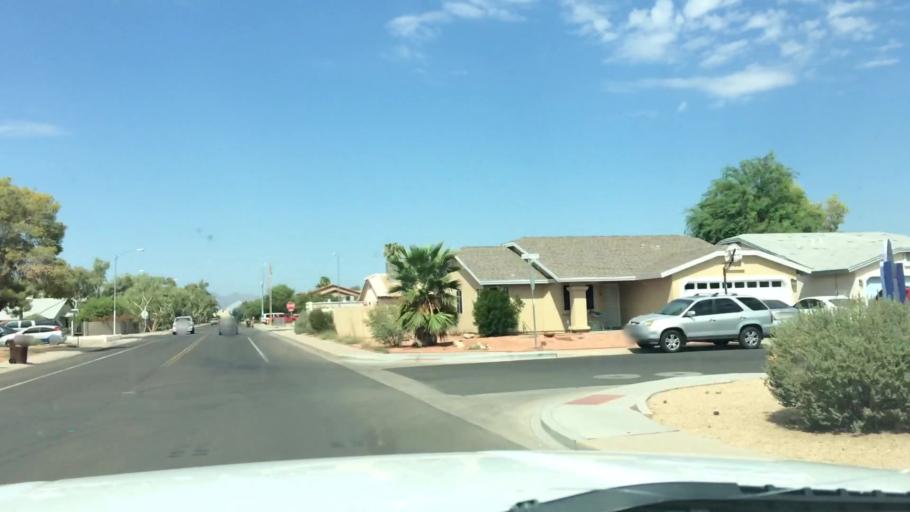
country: US
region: Arizona
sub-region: Maricopa County
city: Peoria
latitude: 33.5773
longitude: -112.2497
